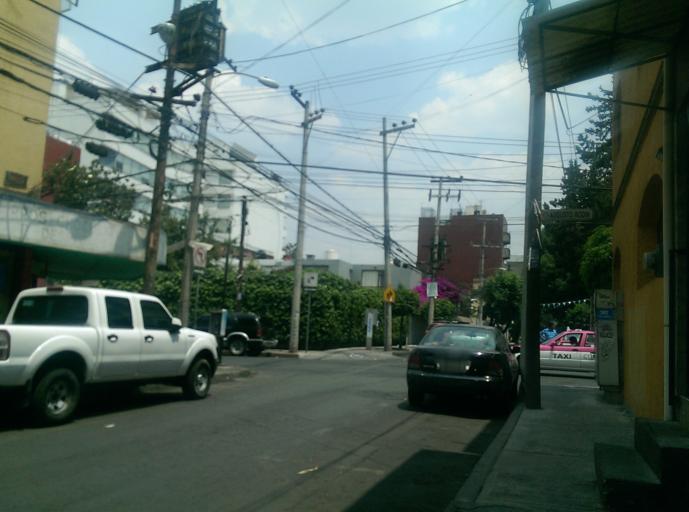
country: MX
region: Mexico City
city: Colonia del Valle
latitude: 19.3754
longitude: -99.1831
